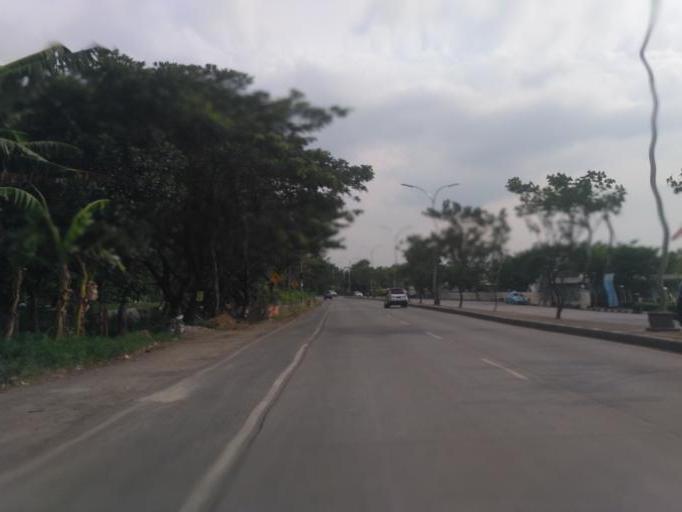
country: ID
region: Central Java
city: Semarang
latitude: -6.9718
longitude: 110.3895
